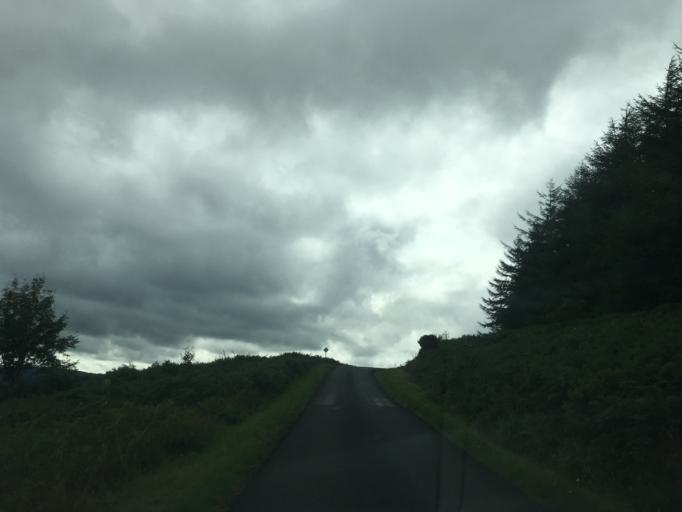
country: GB
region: Scotland
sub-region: Argyll and Bute
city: Tarbert
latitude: 55.8715
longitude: -5.2870
